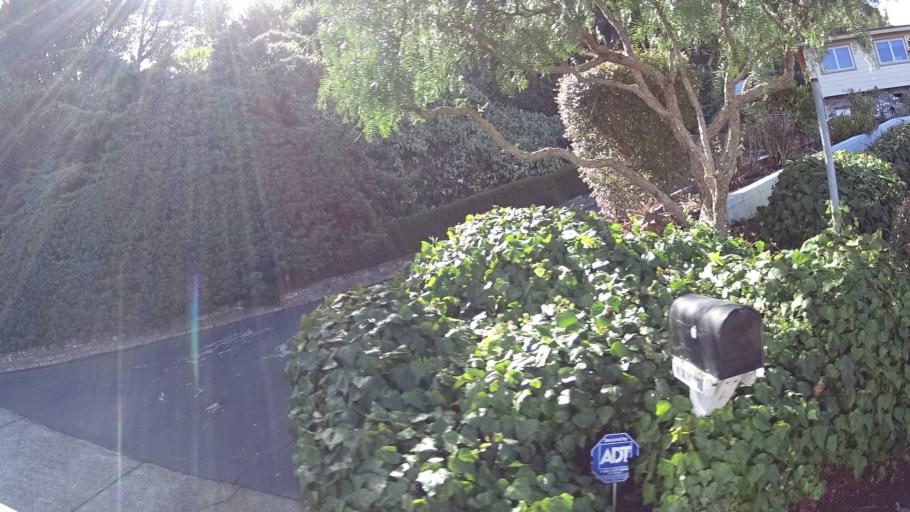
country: US
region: California
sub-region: San Mateo County
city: Brisbane
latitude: 37.6815
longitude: -122.4074
